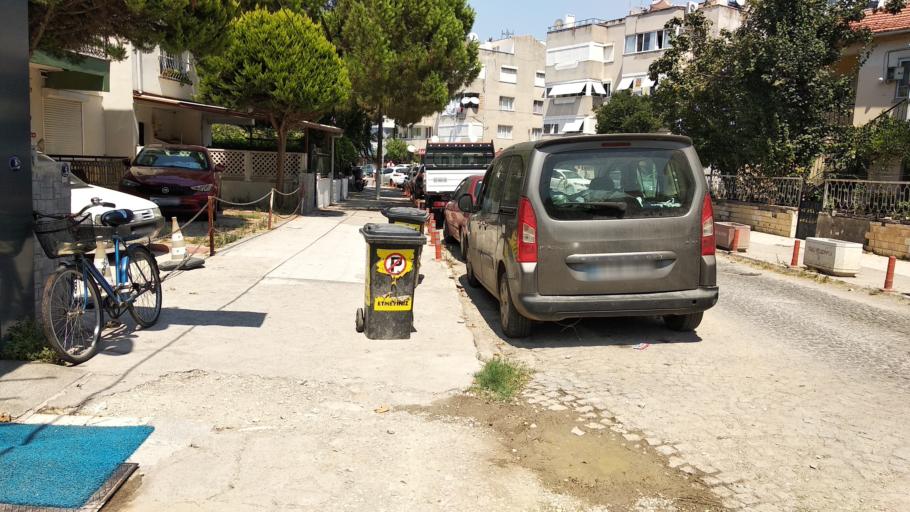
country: TR
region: Izmir
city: Dikili
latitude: 39.0736
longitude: 26.8901
